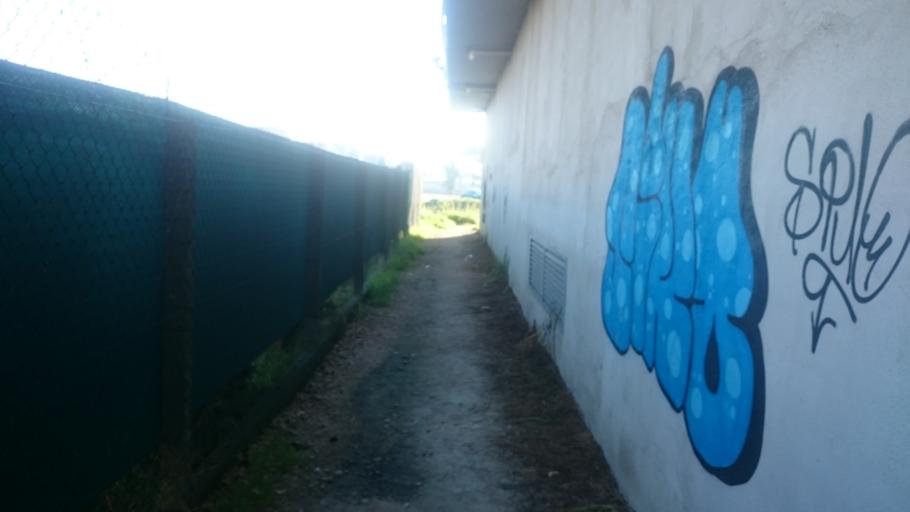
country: ES
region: Galicia
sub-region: Provincia de Pontevedra
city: Porrino
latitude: 42.1585
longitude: -8.6220
